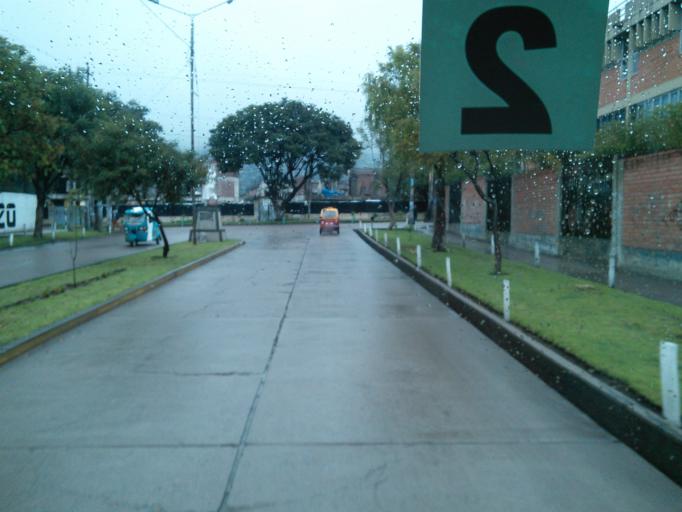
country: PE
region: Ayacucho
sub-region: Provincia de Huamanga
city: Ayacucho
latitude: -13.1498
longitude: -74.2221
